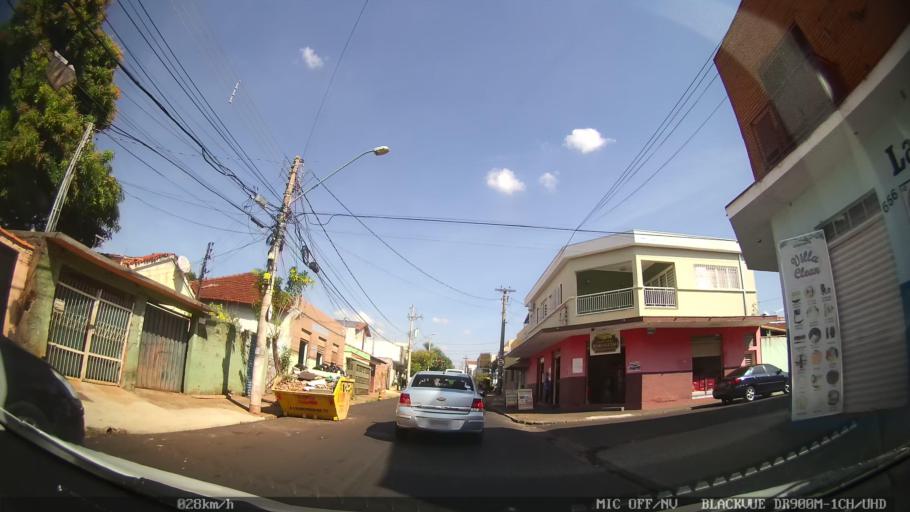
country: BR
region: Sao Paulo
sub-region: Ribeirao Preto
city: Ribeirao Preto
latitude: -21.1832
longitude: -47.8252
